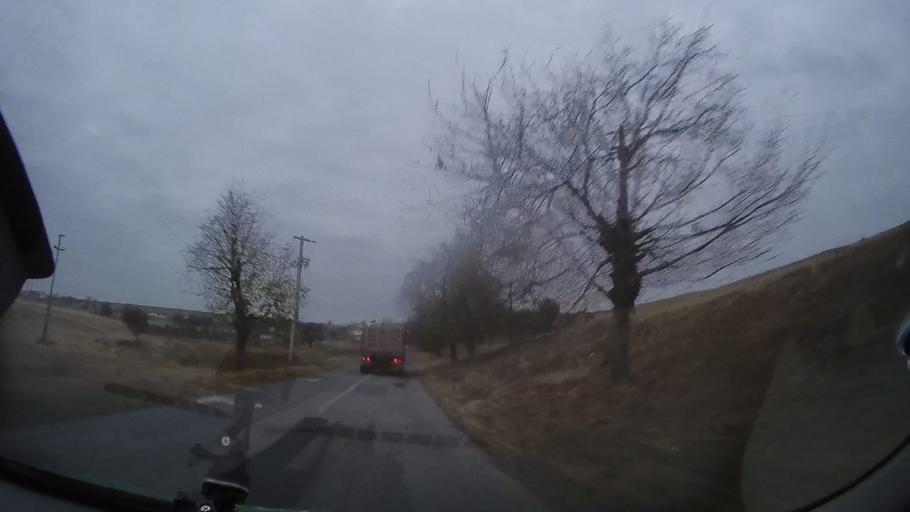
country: RO
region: Tulcea
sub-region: Comuna Mihai Bravu
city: Mihai Bravu
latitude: 44.9578
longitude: 28.6494
